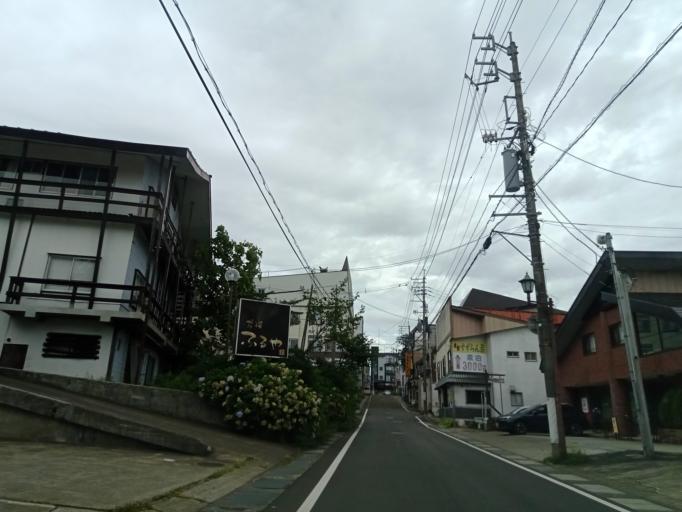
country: JP
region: Niigata
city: Arai
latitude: 36.8928
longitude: 138.1775
